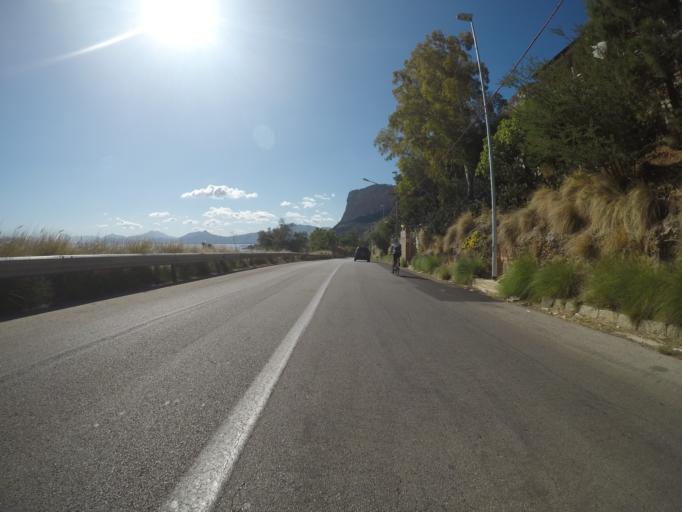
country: IT
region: Sicily
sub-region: Palermo
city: Palermo
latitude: 38.1746
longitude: 13.3661
